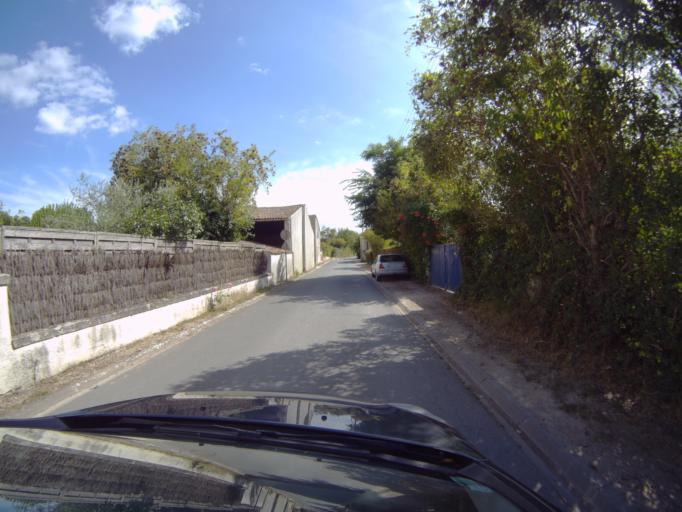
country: FR
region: Poitou-Charentes
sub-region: Departement des Deux-Sevres
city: Saint-Hilaire-la-Palud
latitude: 46.2759
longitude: -0.6560
